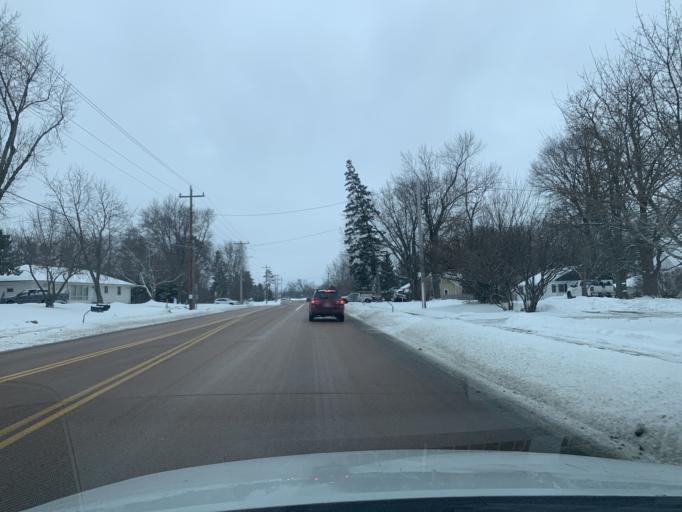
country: US
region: Minnesota
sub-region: Carver County
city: Victoria
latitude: 44.8533
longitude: -93.6602
